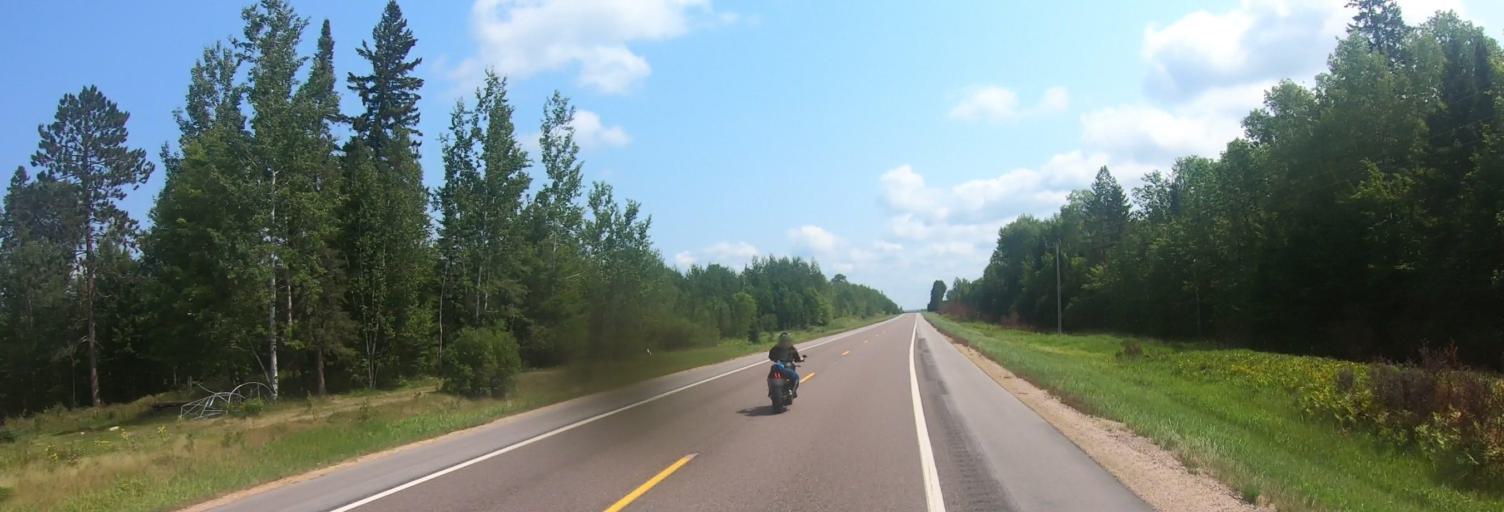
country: US
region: Minnesota
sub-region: Saint Louis County
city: Mountain Iron
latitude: 48.0596
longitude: -92.7533
